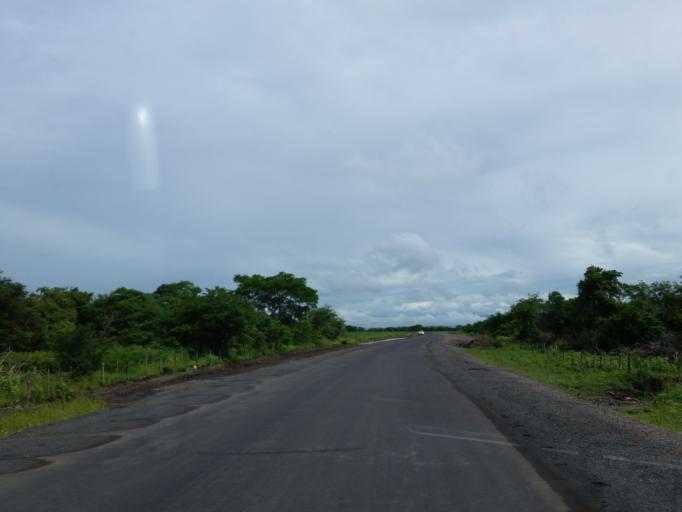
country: NI
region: Leon
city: La Paz Centro
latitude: 12.4913
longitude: -86.6118
